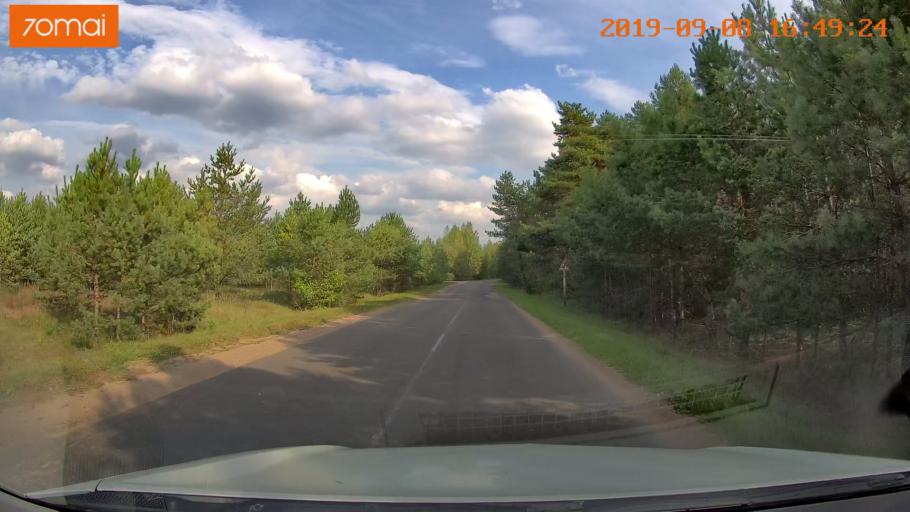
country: BY
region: Grodnenskaya
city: Hrodna
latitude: 53.8100
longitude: 23.8730
